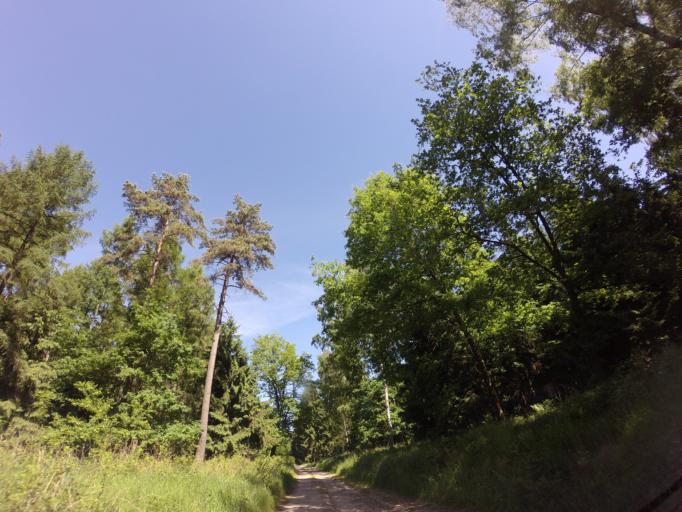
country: PL
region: West Pomeranian Voivodeship
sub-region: Powiat choszczenski
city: Recz
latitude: 53.3095
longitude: 15.6022
